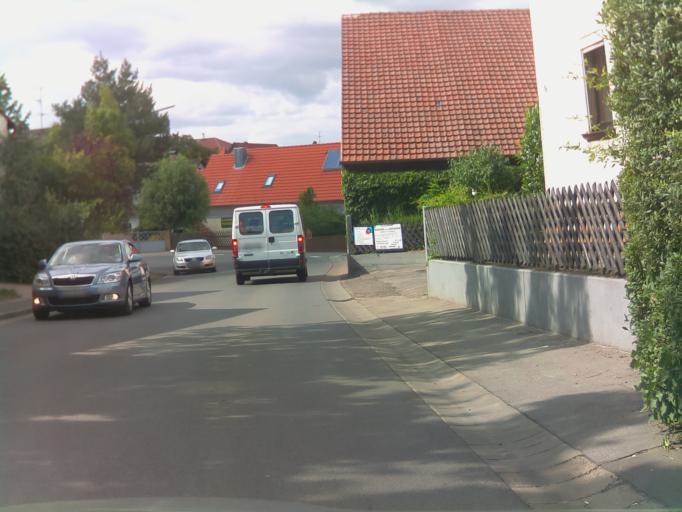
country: DE
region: Bavaria
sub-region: Regierungsbezirk Unterfranken
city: Knetzgau
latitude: 49.9928
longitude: 10.5497
